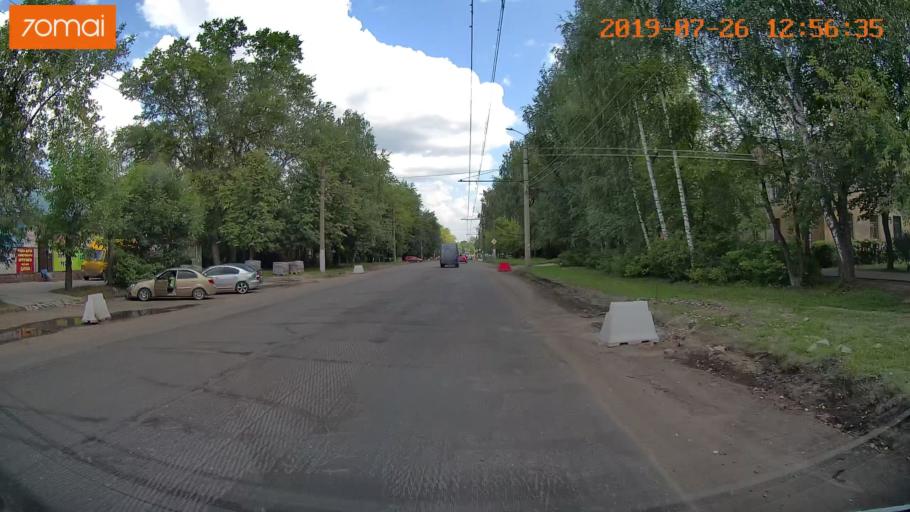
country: RU
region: Ivanovo
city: Bogorodskoye
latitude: 57.0169
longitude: 41.0133
